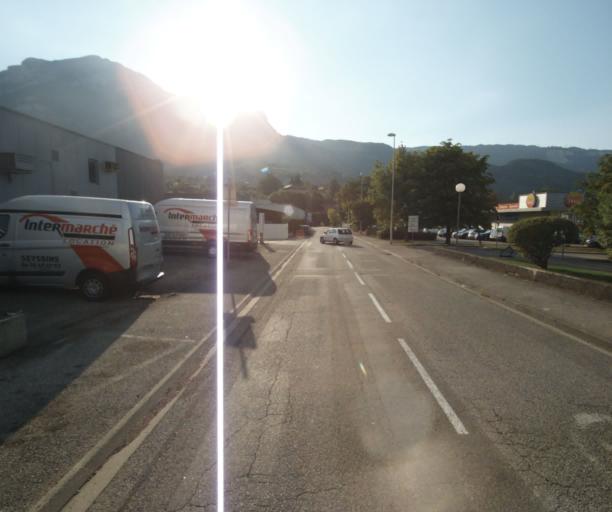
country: FR
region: Rhone-Alpes
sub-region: Departement de l'Isere
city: Seyssinet-Pariset
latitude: 45.1607
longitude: 5.6962
